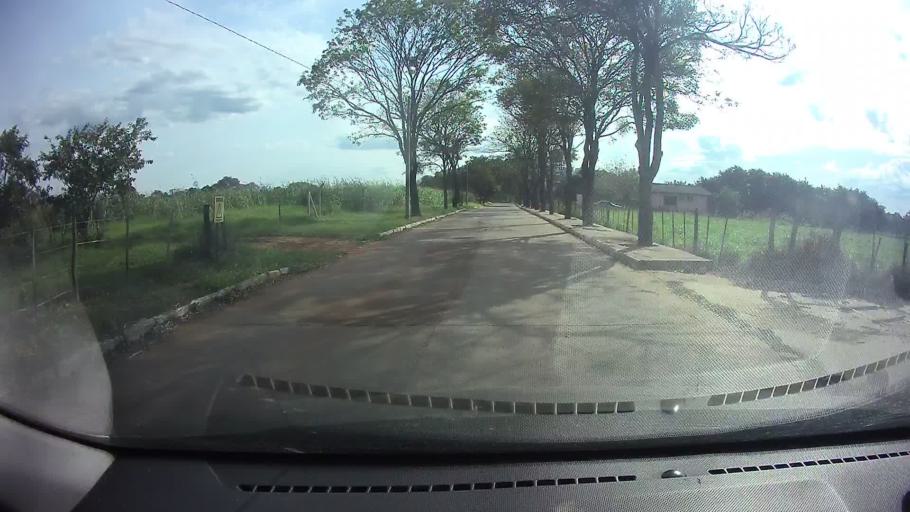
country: PY
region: Central
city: Fernando de la Mora
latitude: -25.3283
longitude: -57.5239
